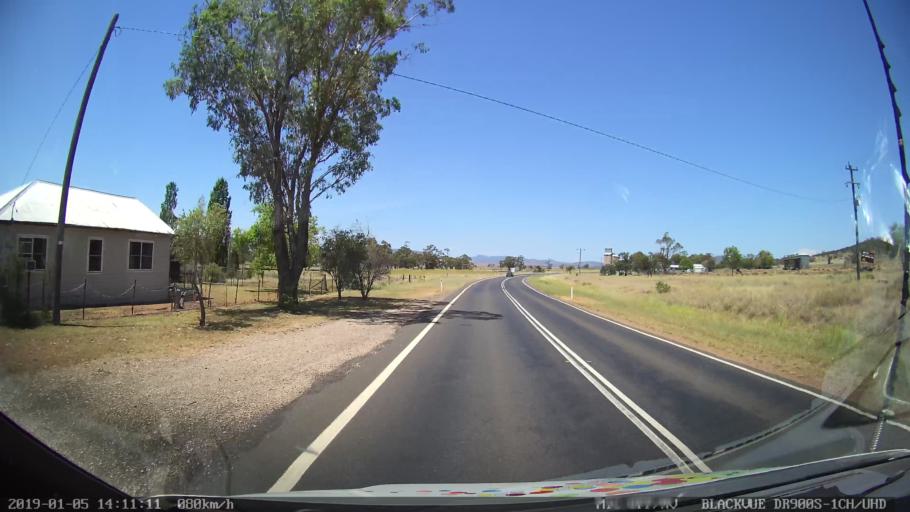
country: AU
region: New South Wales
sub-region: Gunnedah
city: Gunnedah
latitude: -31.2440
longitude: 150.4545
